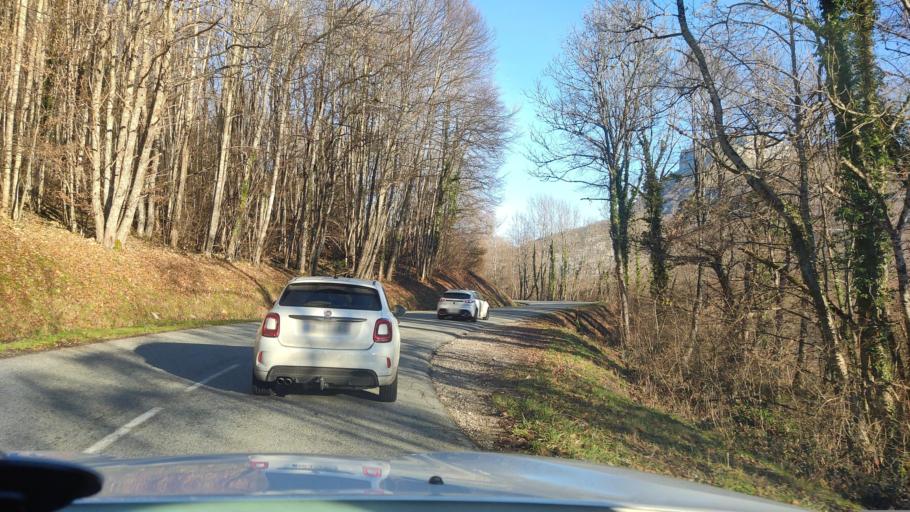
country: FR
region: Rhone-Alpes
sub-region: Departement de la Savoie
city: Barby
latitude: 45.6007
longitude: 6.0164
